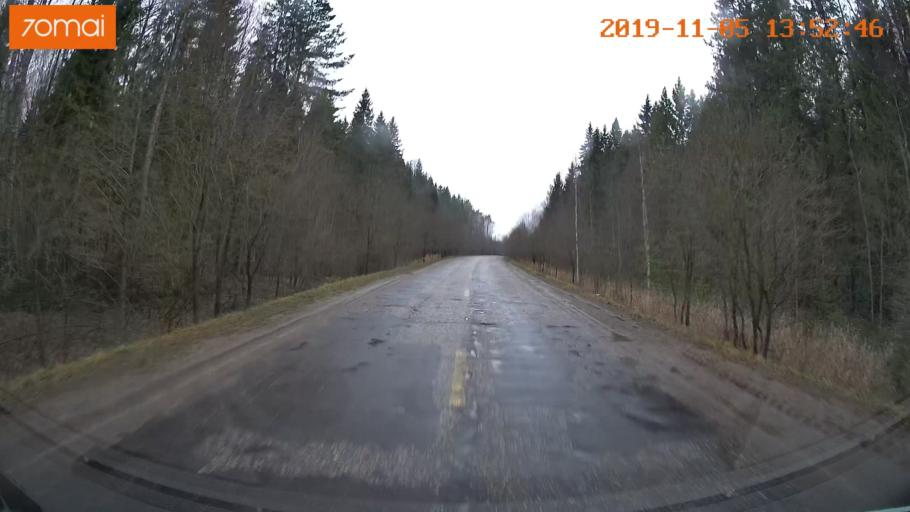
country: RU
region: Ivanovo
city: Kaminskiy
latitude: 57.0289
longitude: 41.3811
